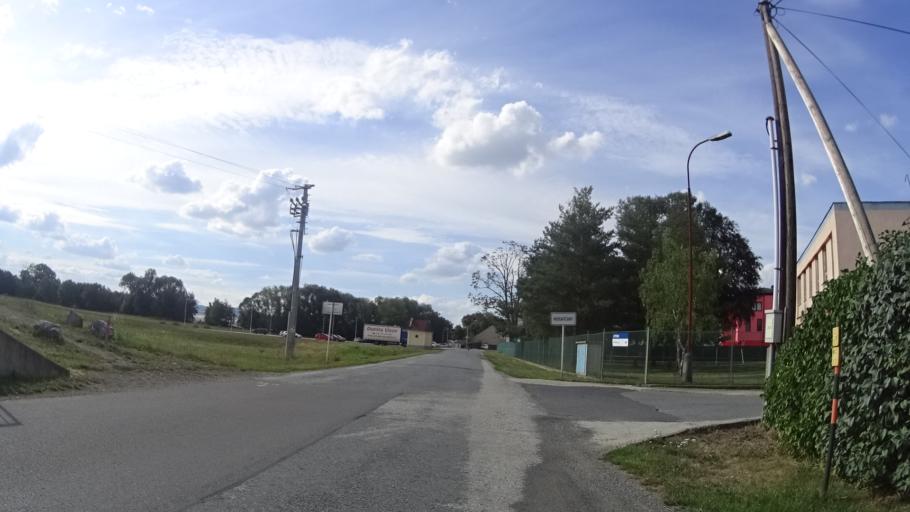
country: CZ
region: Olomoucky
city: Moravicany
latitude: 49.7526
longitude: 16.9663
